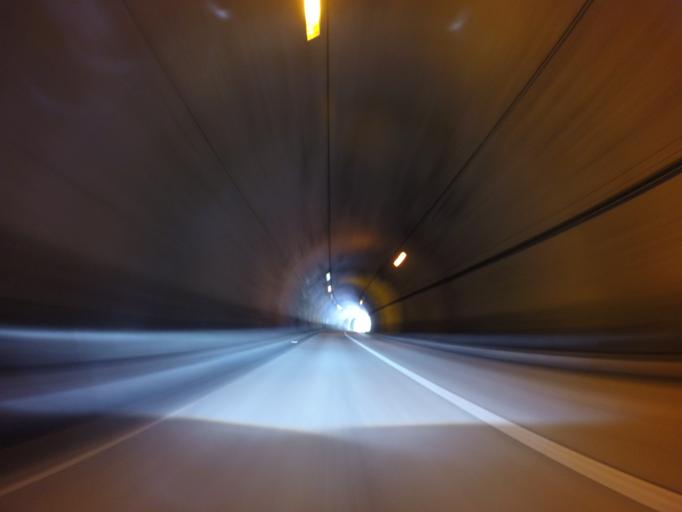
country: JP
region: Shizuoka
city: Shizuoka-shi
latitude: 35.2260
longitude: 138.3469
